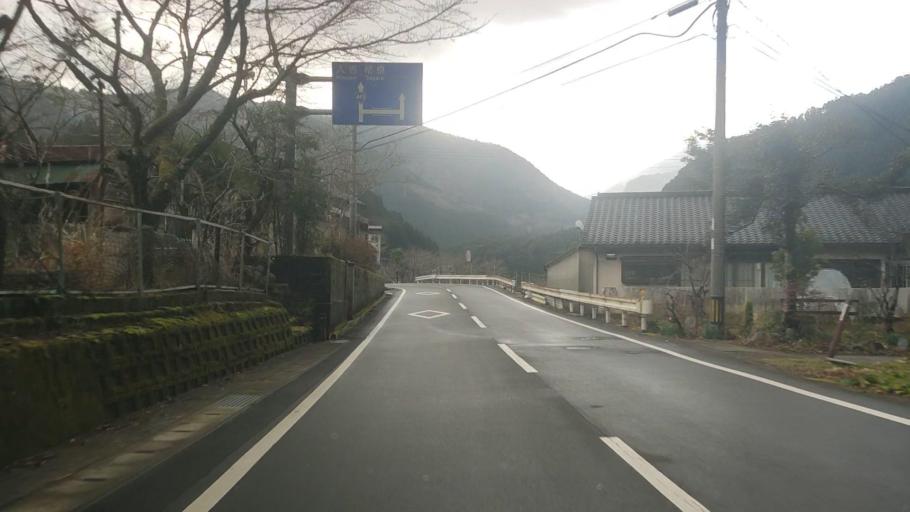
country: JP
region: Kumamoto
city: Hitoyoshi
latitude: 32.4420
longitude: 130.8561
